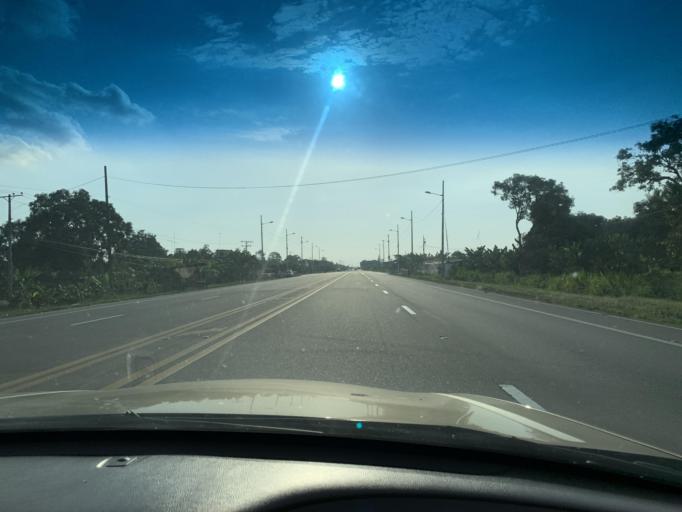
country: EC
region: Guayas
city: Naranjito
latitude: -2.2568
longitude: -79.5857
